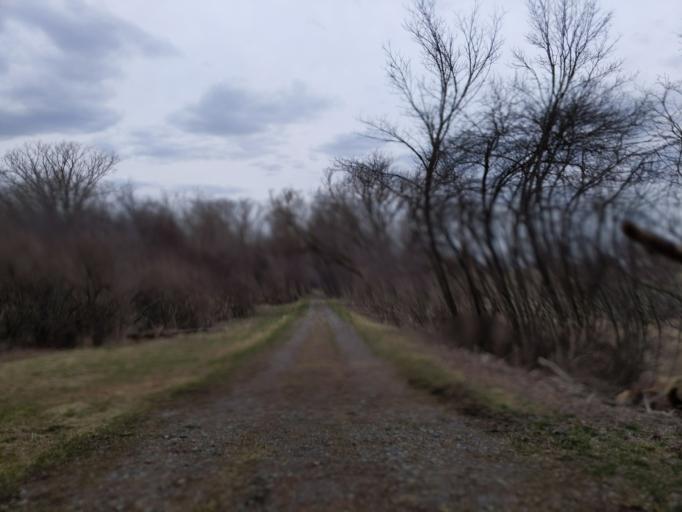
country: US
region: New York
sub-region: Tompkins County
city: Dryden
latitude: 42.5016
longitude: -76.3364
